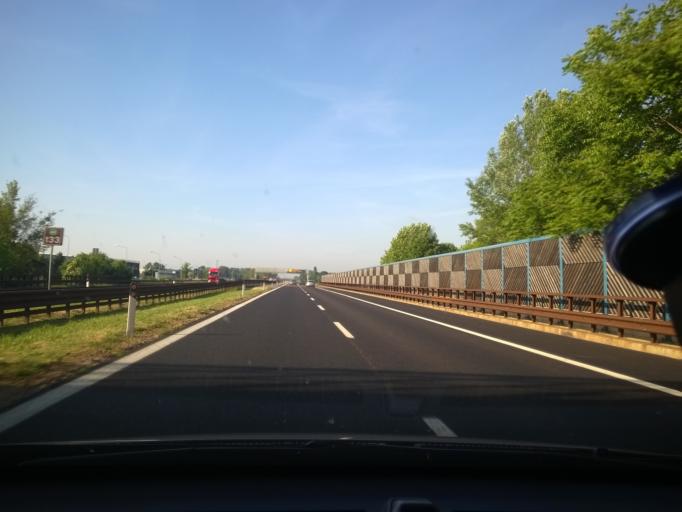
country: IT
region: Emilia-Romagna
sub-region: Provincia di Modena
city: Santa Croce Scuole
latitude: 44.7857
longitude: 10.8502
